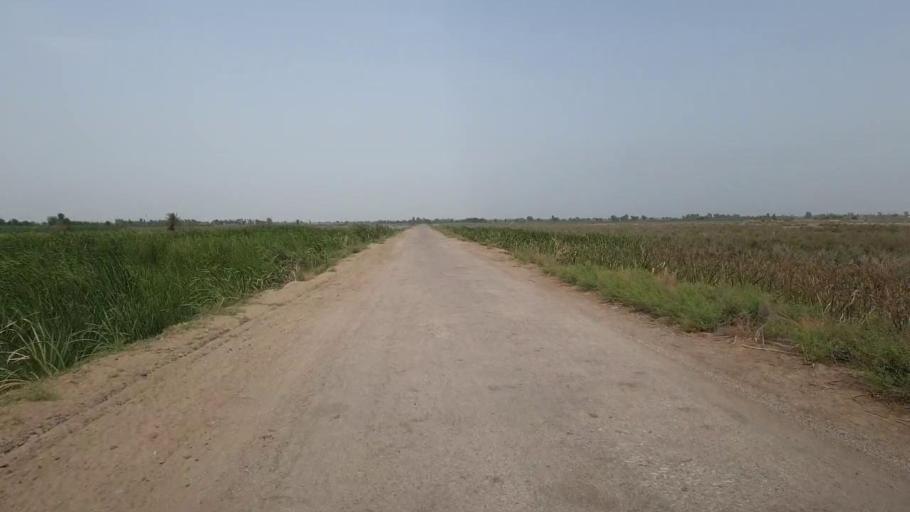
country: PK
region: Sindh
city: Daulatpur
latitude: 26.5462
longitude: 68.0793
